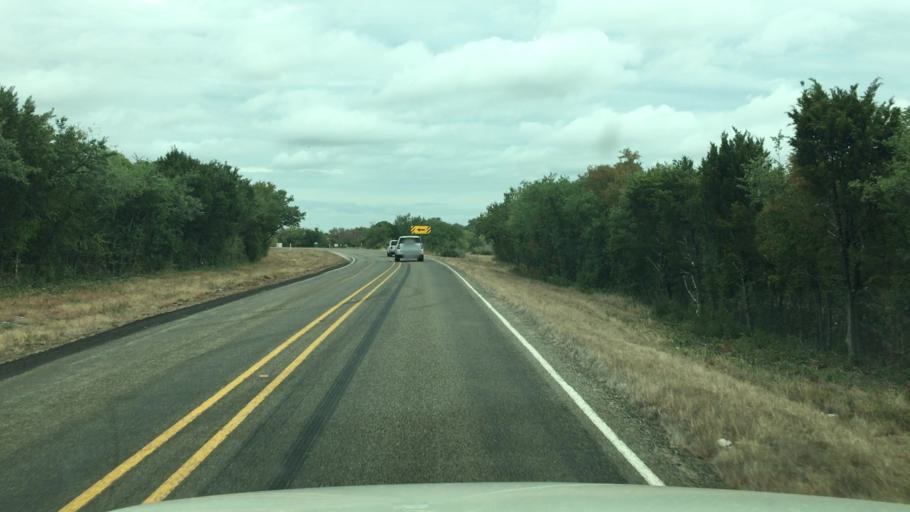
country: US
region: Texas
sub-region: Llano County
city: Horseshoe Bay
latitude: 30.4765
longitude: -98.4170
